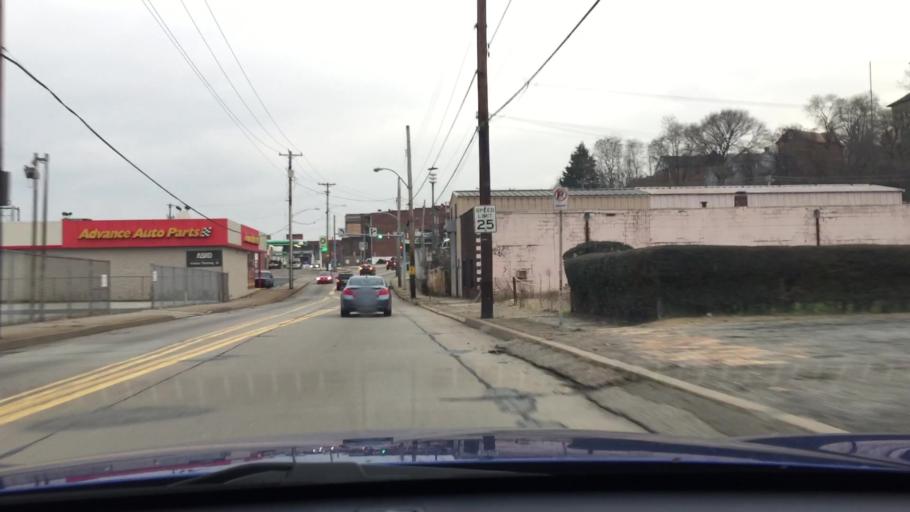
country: US
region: Pennsylvania
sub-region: Allegheny County
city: Homestead
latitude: 40.4015
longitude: -79.9190
